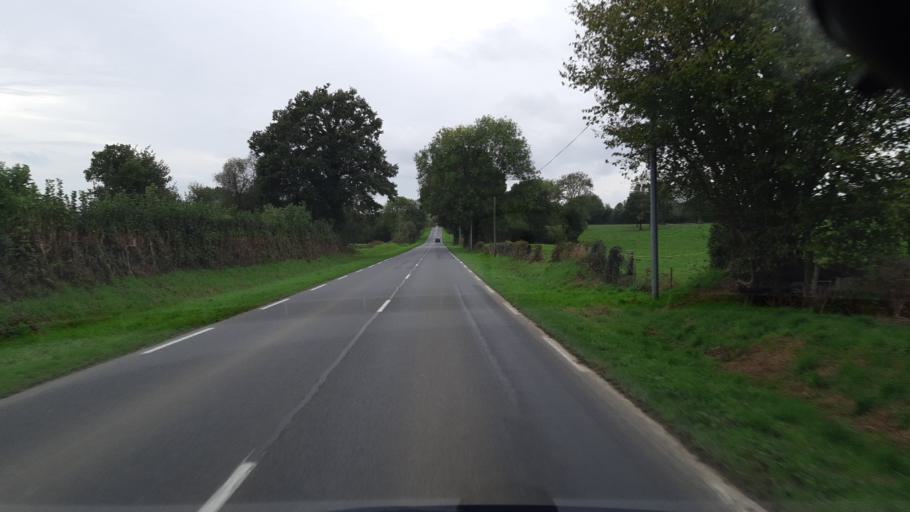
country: FR
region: Lower Normandy
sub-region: Departement de la Manche
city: Gavray
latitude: 48.9395
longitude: -1.3351
